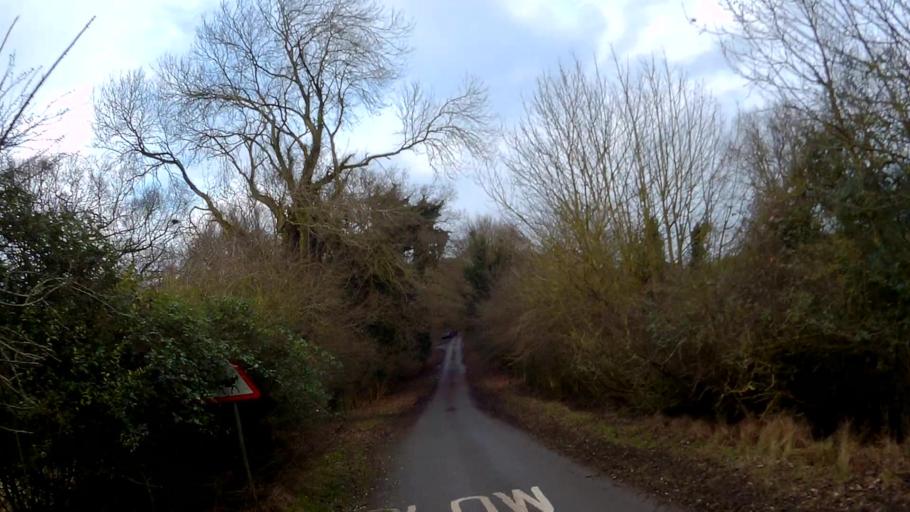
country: GB
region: England
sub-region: Lincolnshire
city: Bourne
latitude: 52.8171
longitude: -0.4372
